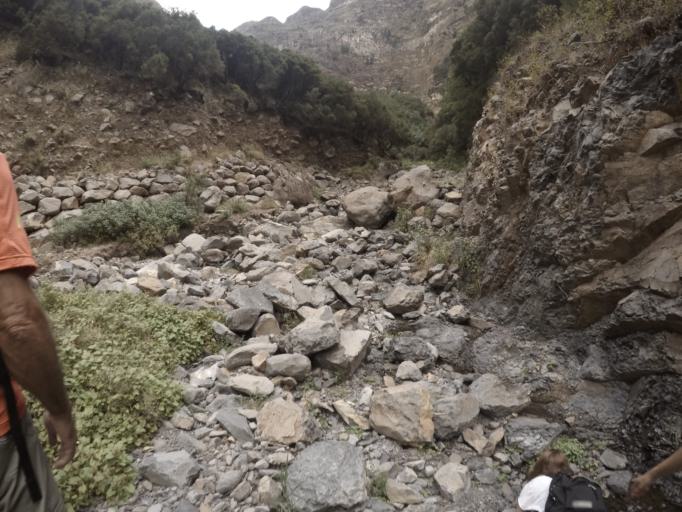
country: PT
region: Madeira
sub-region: Funchal
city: Nossa Senhora do Monte
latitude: 32.7026
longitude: -16.9205
